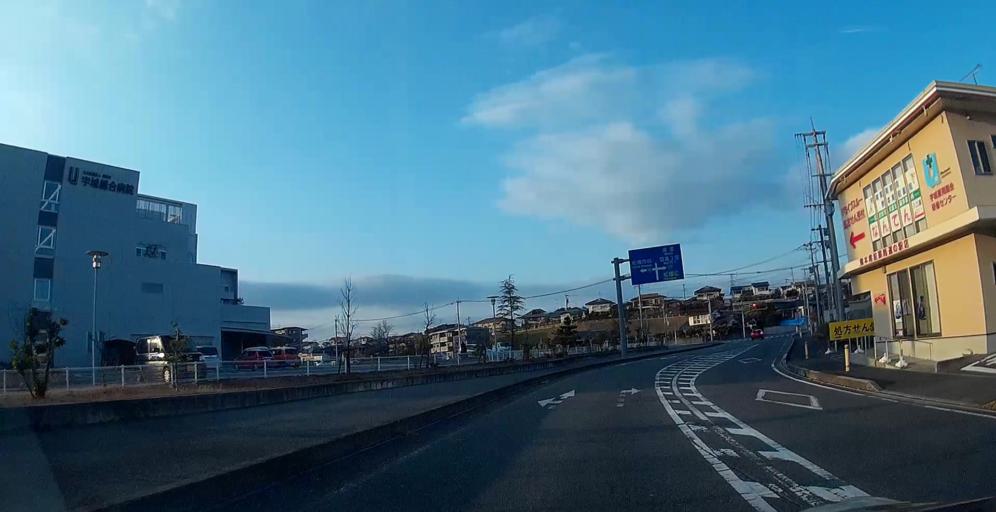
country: JP
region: Kumamoto
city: Matsubase
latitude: 32.6508
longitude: 130.6975
